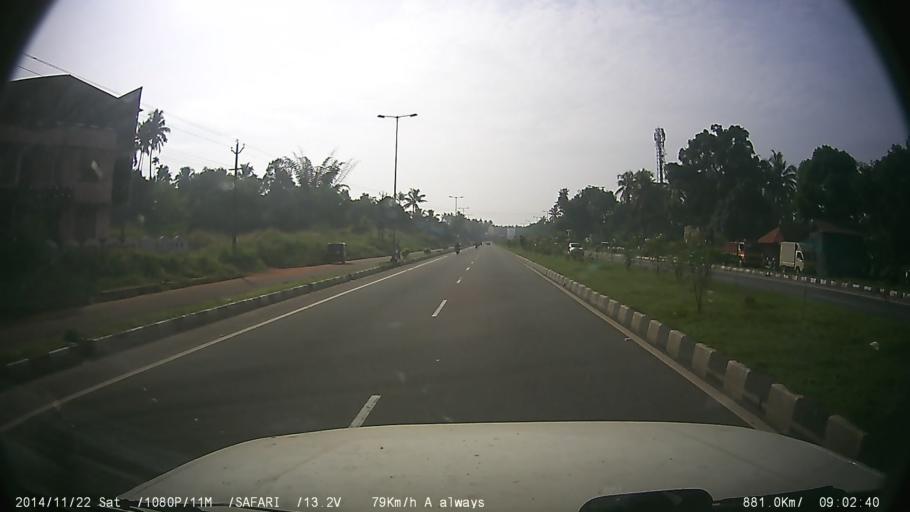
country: IN
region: Kerala
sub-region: Thrissur District
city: Kizhake Chalakudi
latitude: 10.3671
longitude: 76.3144
